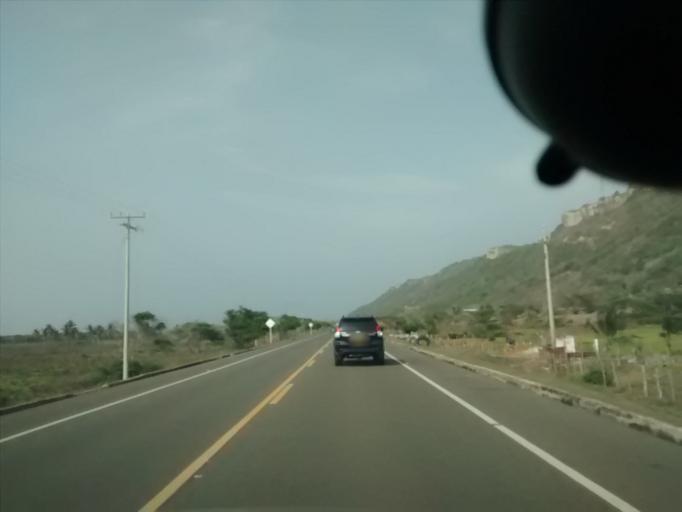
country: CO
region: Bolivar
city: Clemencia
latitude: 10.6225
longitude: -75.4459
